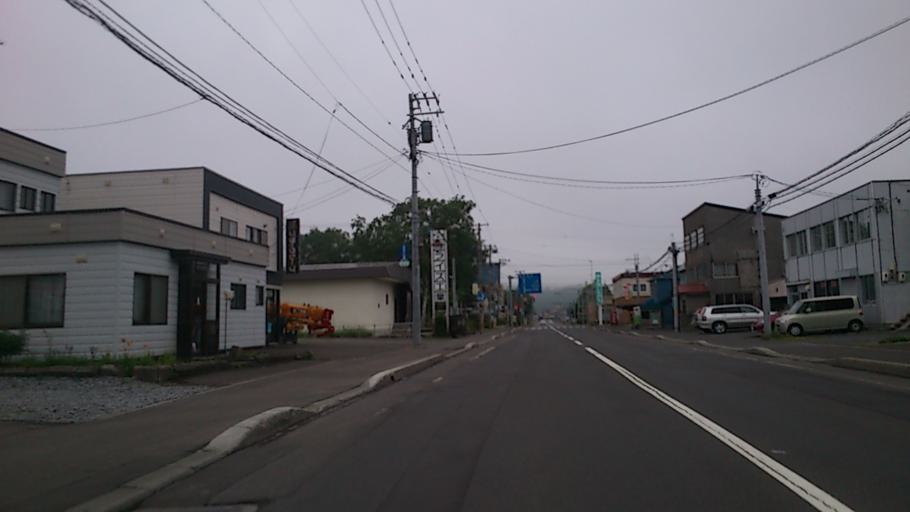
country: JP
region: Hokkaido
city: Niseko Town
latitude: 42.8592
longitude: 140.8858
